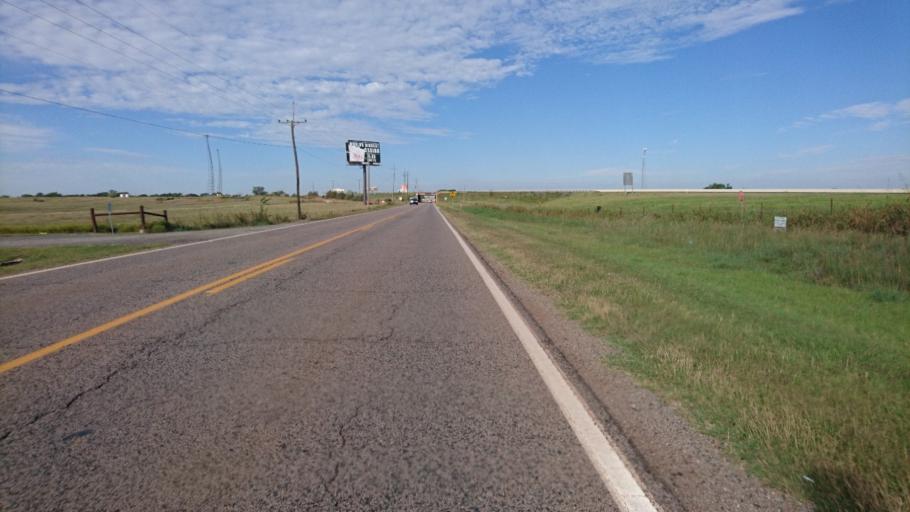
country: US
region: Oklahoma
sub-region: Oklahoma County
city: Luther
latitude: 35.6811
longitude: -97.0432
